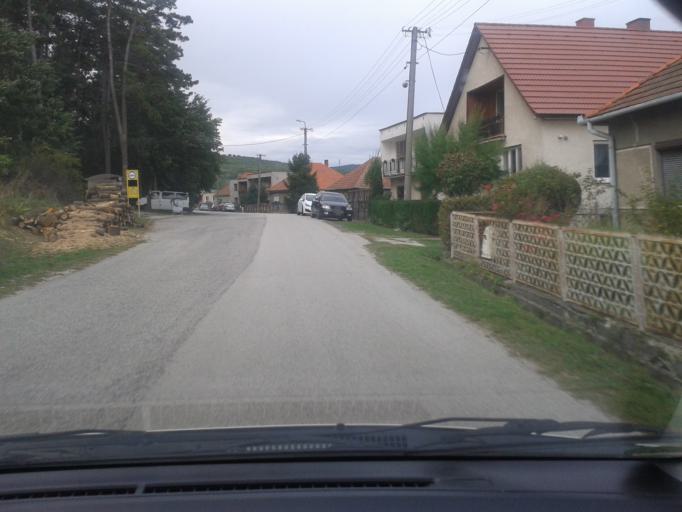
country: SK
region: Nitriansky
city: Zlate Moravce
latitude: 48.4314
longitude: 18.3252
